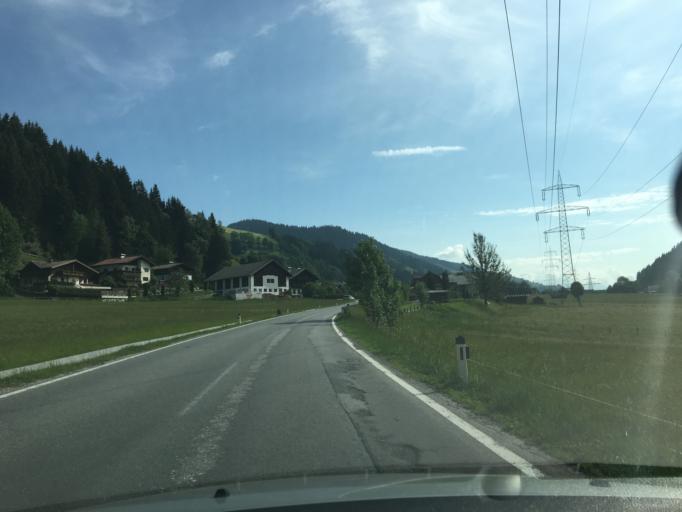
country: AT
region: Salzburg
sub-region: Politischer Bezirk Sankt Johann im Pongau
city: Wagrain
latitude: 47.3489
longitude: 13.3107
